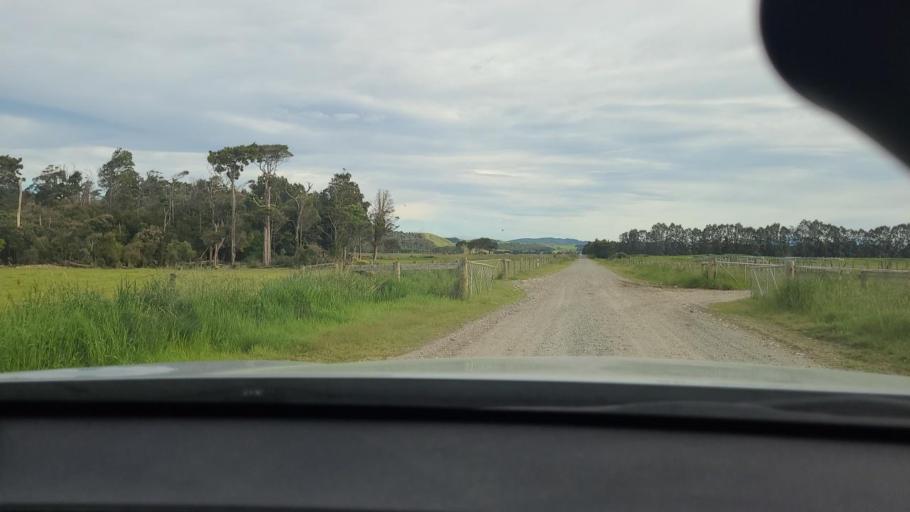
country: NZ
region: Southland
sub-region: Southland District
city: Riverton
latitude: -46.1693
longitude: 167.6235
